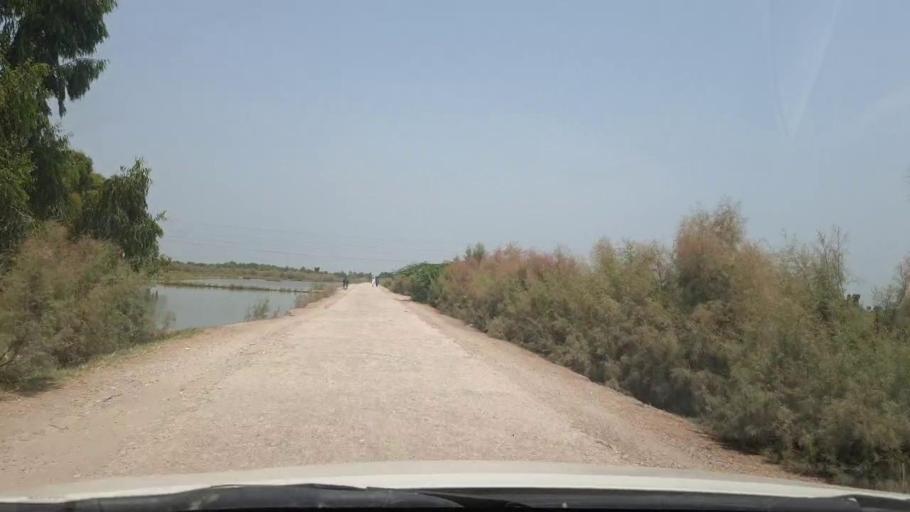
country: PK
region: Sindh
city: Rustam jo Goth
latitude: 28.0253
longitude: 68.8129
